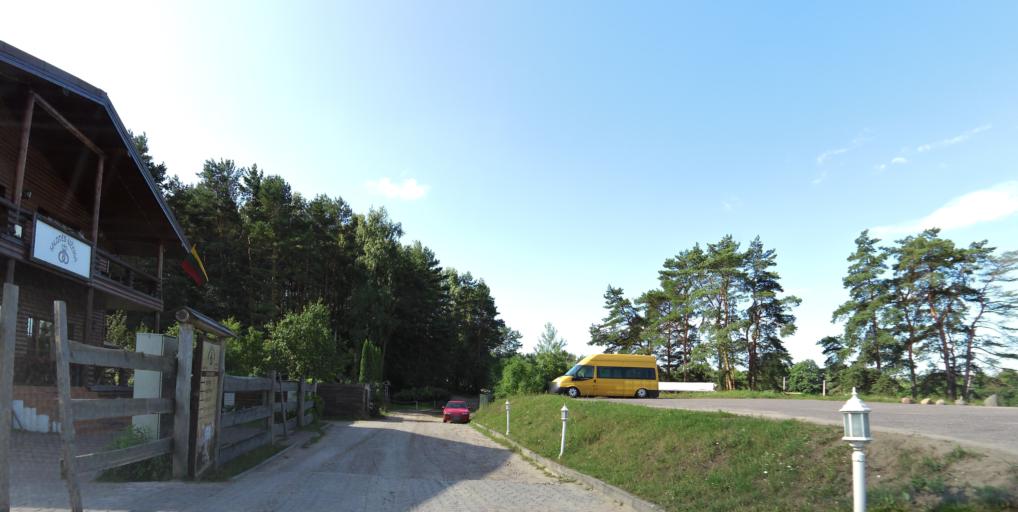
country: LT
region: Vilnius County
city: Pilaite
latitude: 54.6959
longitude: 25.1811
